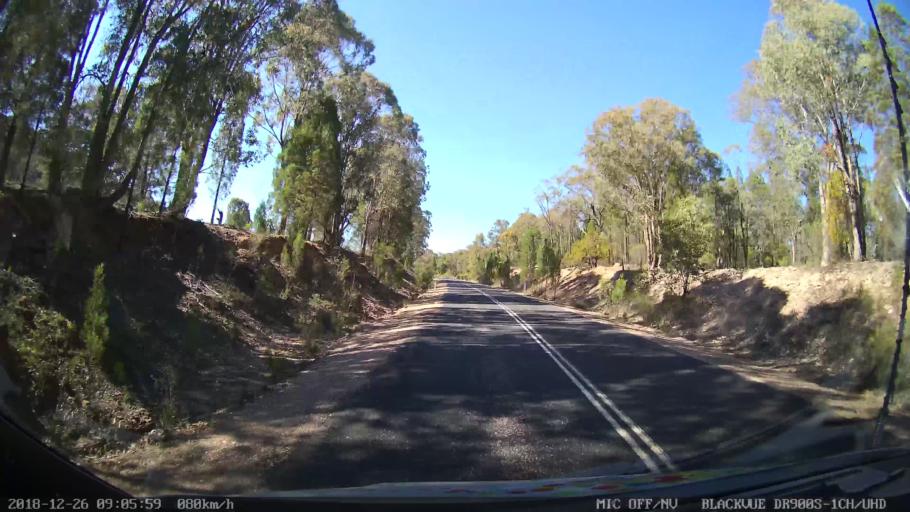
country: AU
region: New South Wales
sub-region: Mid-Western Regional
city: Kandos
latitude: -32.6887
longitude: 150.0047
